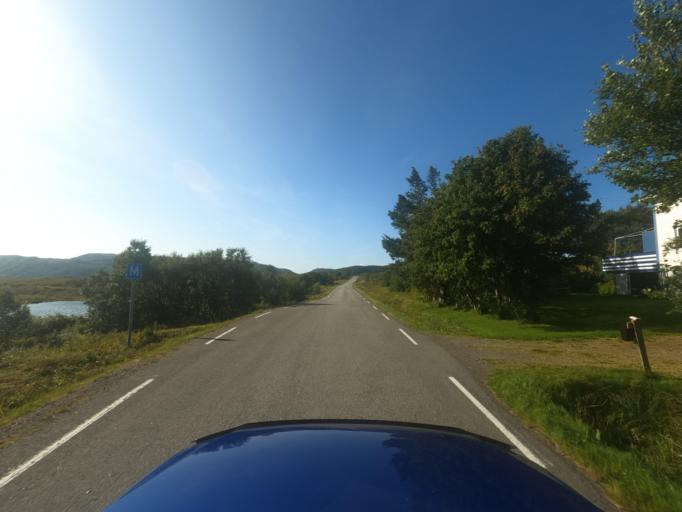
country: NO
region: Nordland
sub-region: Vestvagoy
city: Evjen
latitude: 68.3111
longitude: 13.8855
